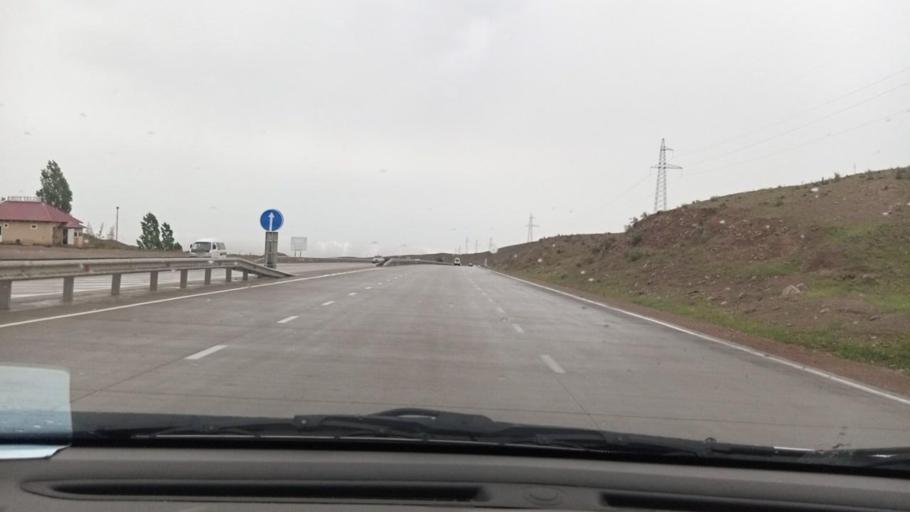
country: UZ
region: Namangan
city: Pop Shahri
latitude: 40.9411
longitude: 70.6897
